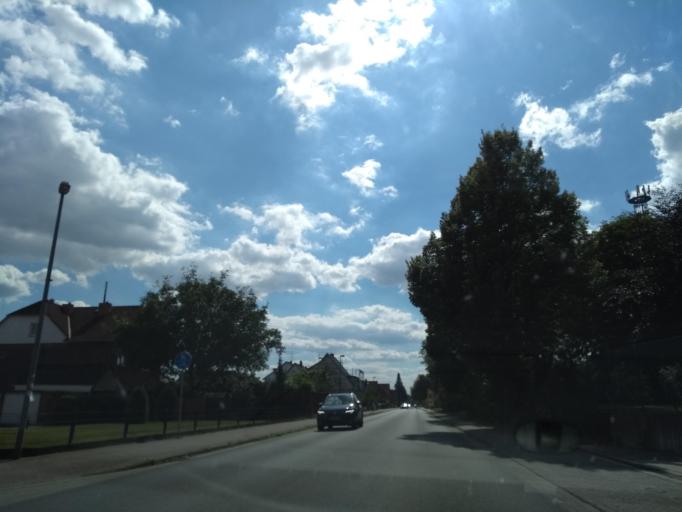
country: DE
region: Lower Saxony
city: Haste
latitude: 52.3840
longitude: 9.3961
